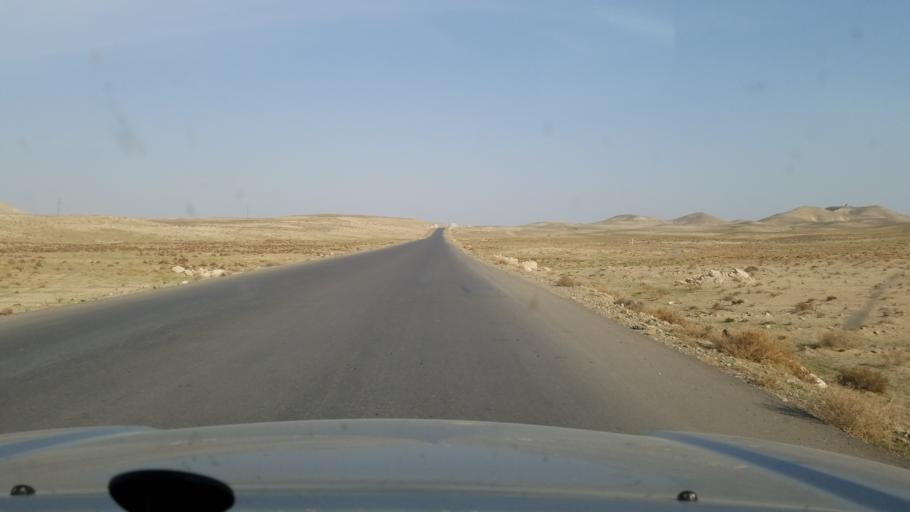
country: AF
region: Jowzjan
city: Khamyab
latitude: 37.6217
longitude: 65.6978
